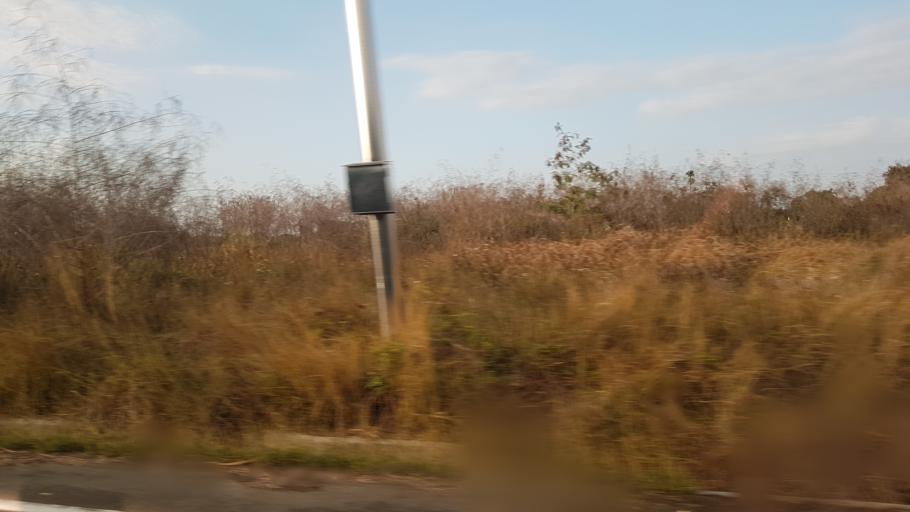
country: TW
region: Taiwan
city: Xinying
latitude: 23.3503
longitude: 120.3769
